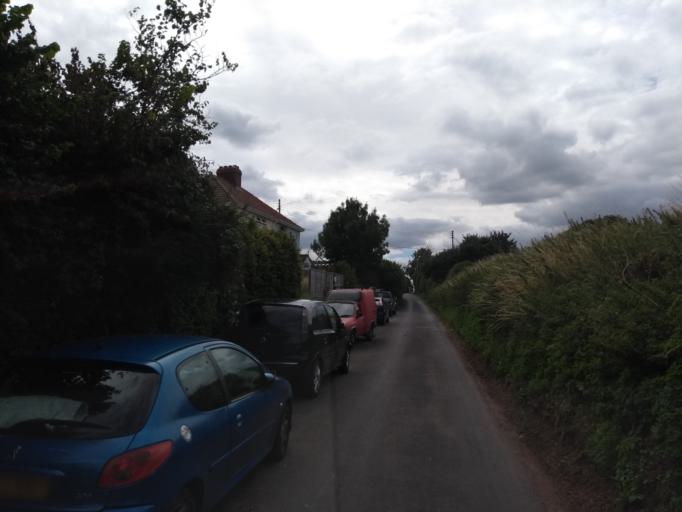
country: GB
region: England
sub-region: Somerset
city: North Petherton
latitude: 51.0884
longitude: -3.0185
